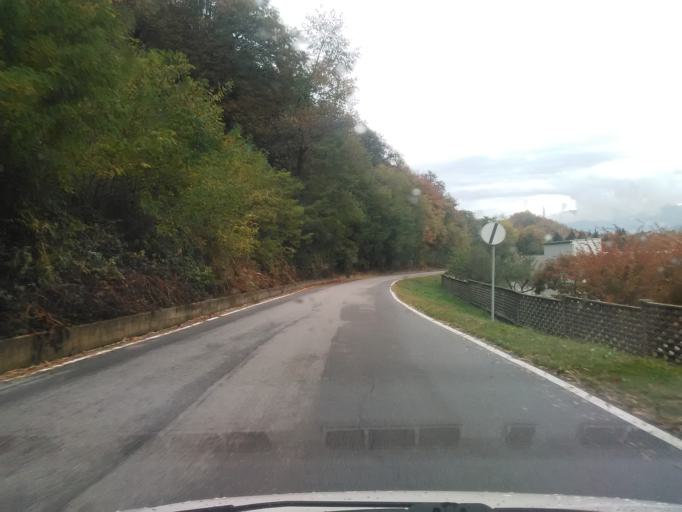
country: IT
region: Piedmont
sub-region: Provincia di Novara
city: Pogno
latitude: 45.7633
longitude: 8.3851
